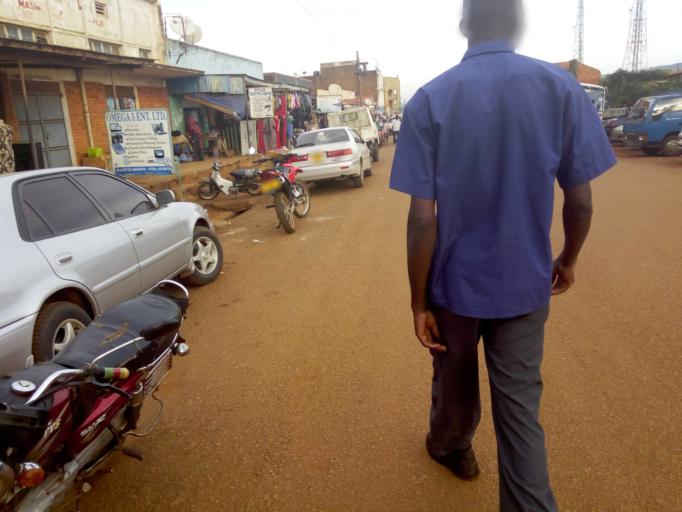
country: UG
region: Western Region
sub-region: Masindi District
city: Masindi
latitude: 1.6827
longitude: 31.7216
